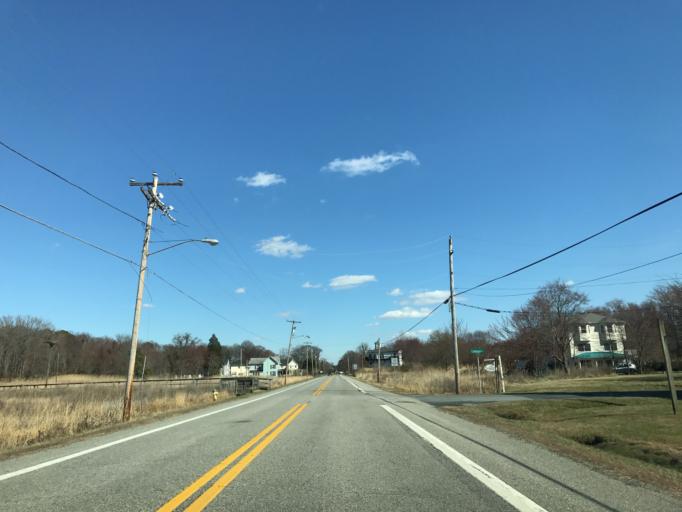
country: US
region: Maryland
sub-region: Kent County
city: Rock Hall
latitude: 39.1406
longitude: -76.2577
